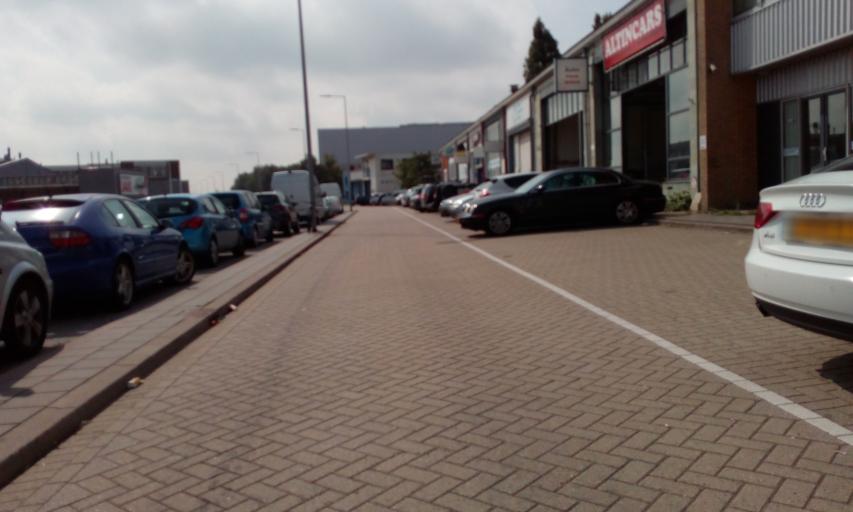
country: NL
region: South Holland
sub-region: Gemeente Schiedam
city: Schiedam
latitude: 51.9111
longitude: 4.4092
